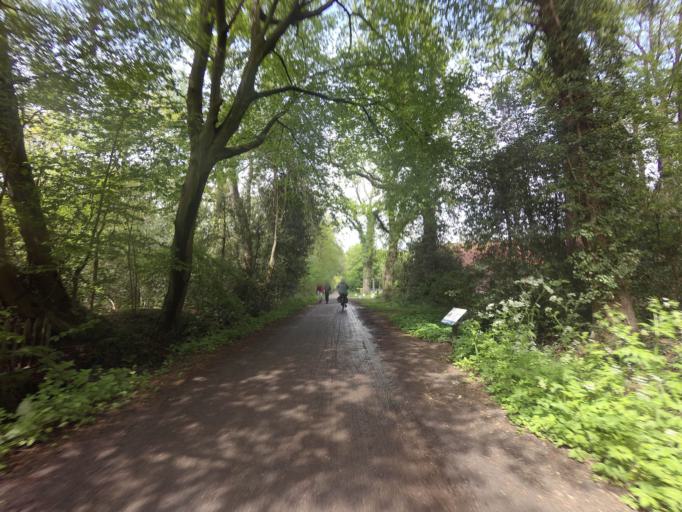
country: NL
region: Overijssel
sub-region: Gemeente Haaksbergen
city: Haaksbergen
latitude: 52.1334
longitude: 6.7217
